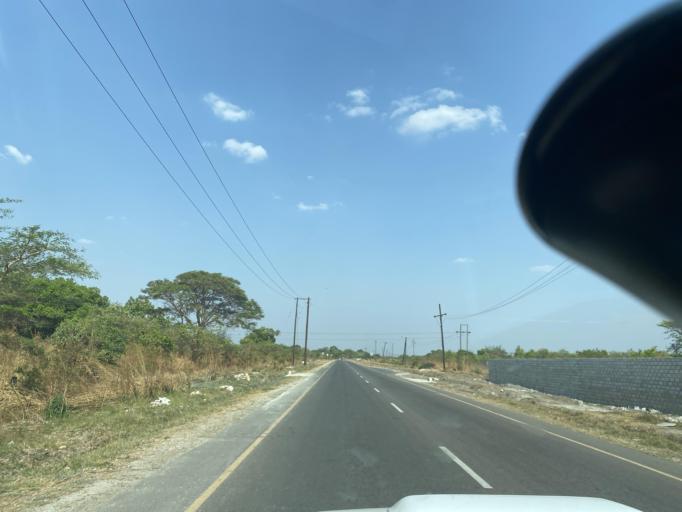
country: ZM
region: Lusaka
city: Lusaka
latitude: -15.3413
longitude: 28.0793
